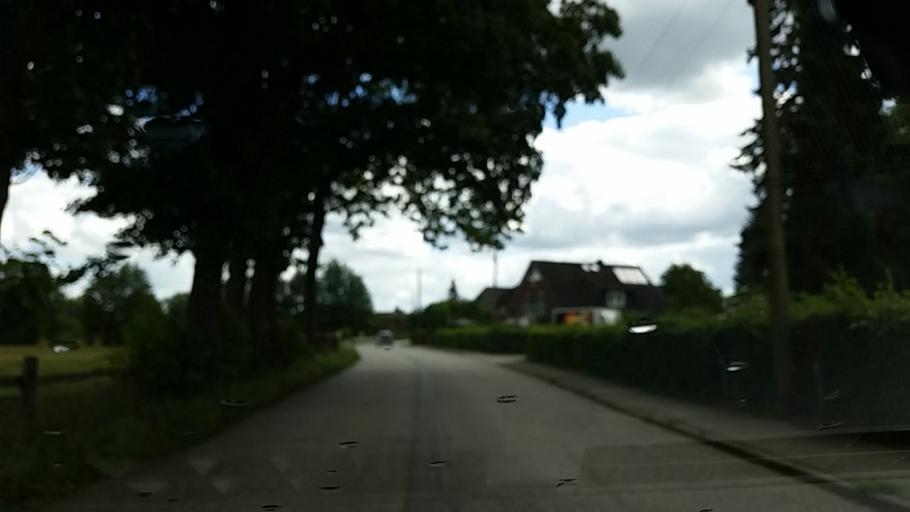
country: DE
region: Schleswig-Holstein
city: Bornsen
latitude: 53.4642
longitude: 10.2644
